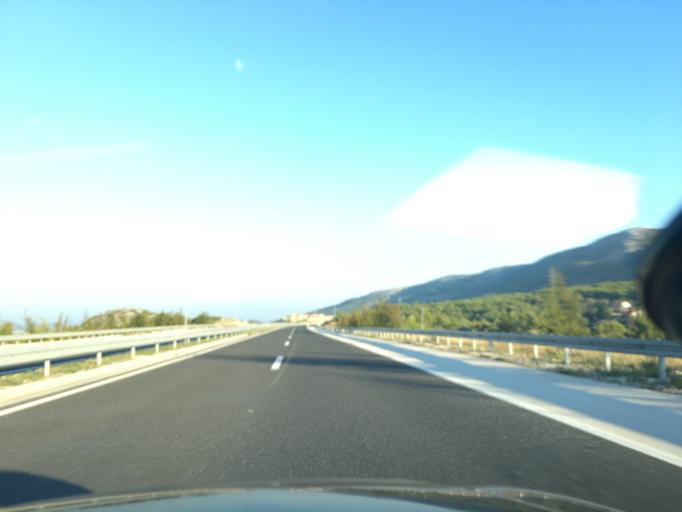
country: HR
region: Sibensko-Kniniska
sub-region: Grad Sibenik
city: Sibenik
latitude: 43.7310
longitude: 15.9749
